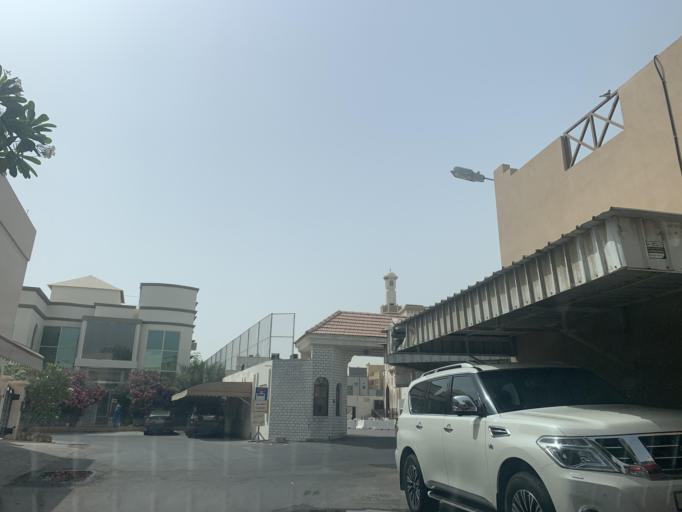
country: BH
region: Northern
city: Ar Rifa'
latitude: 26.1327
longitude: 50.5695
